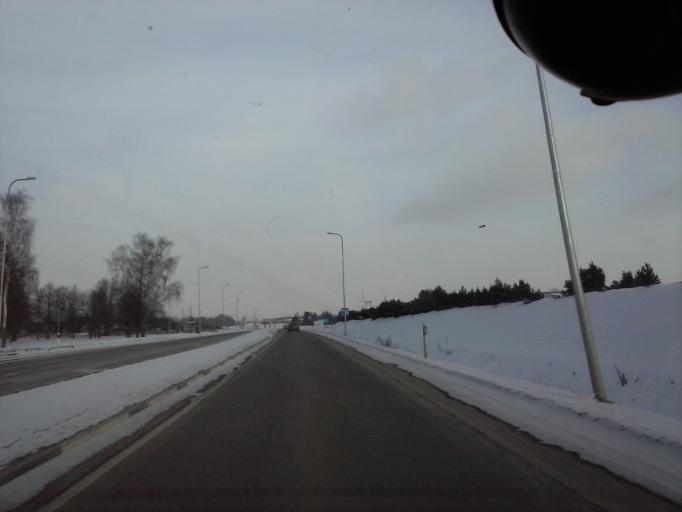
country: EE
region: Tartu
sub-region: Tartu linn
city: Tartu
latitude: 58.3591
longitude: 26.6427
